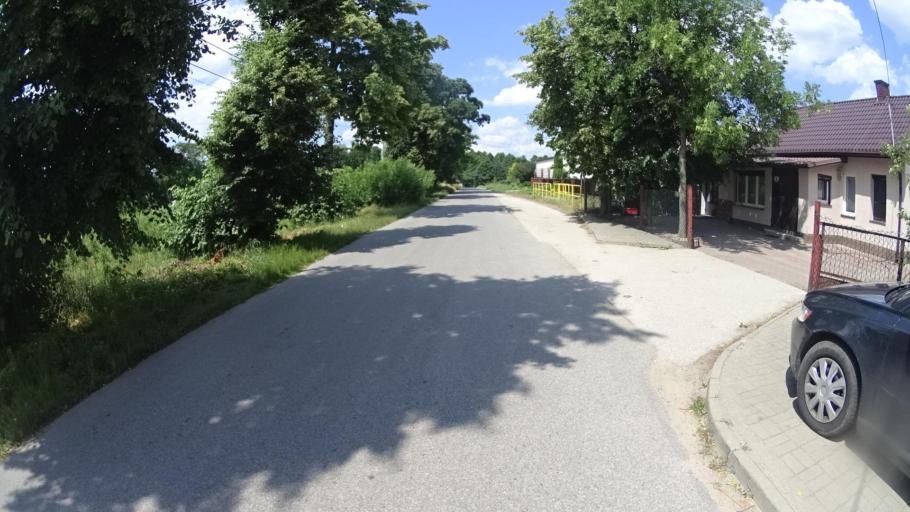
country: PL
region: Masovian Voivodeship
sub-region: Powiat grojecki
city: Goszczyn
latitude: 51.7115
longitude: 20.8880
